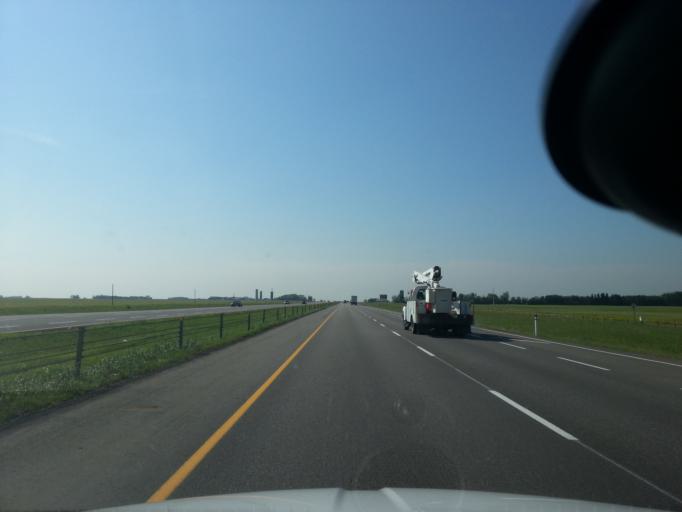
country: CA
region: Alberta
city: Olds
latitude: 51.7354
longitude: -114.0256
